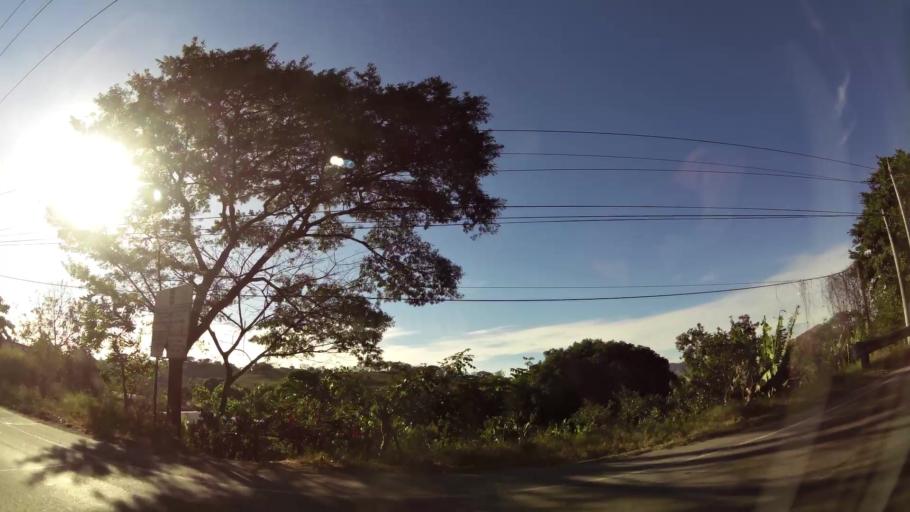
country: SV
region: Santa Ana
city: Metapan
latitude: 14.2995
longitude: -89.4629
